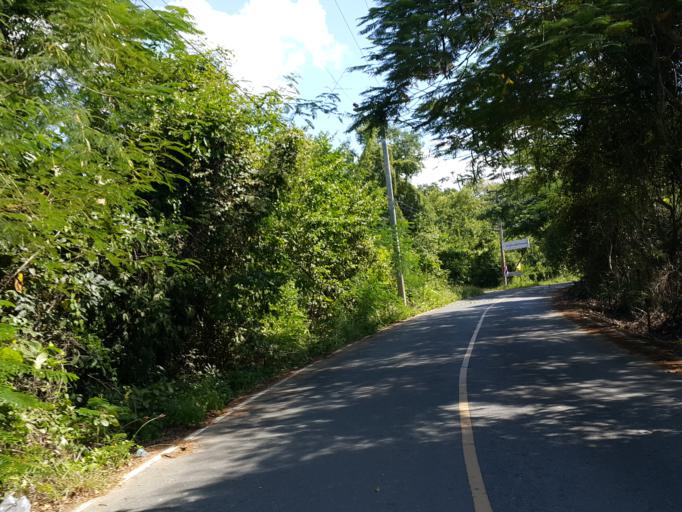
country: TH
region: Chiang Mai
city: San Sai
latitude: 18.8660
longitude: 99.1591
